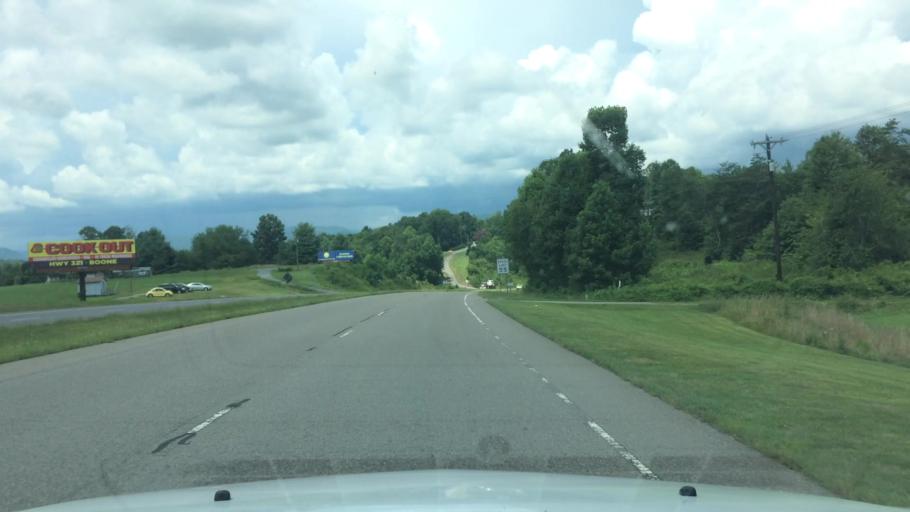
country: US
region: North Carolina
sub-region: Wilkes County
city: Millers Creek
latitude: 36.1431
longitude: -81.2899
